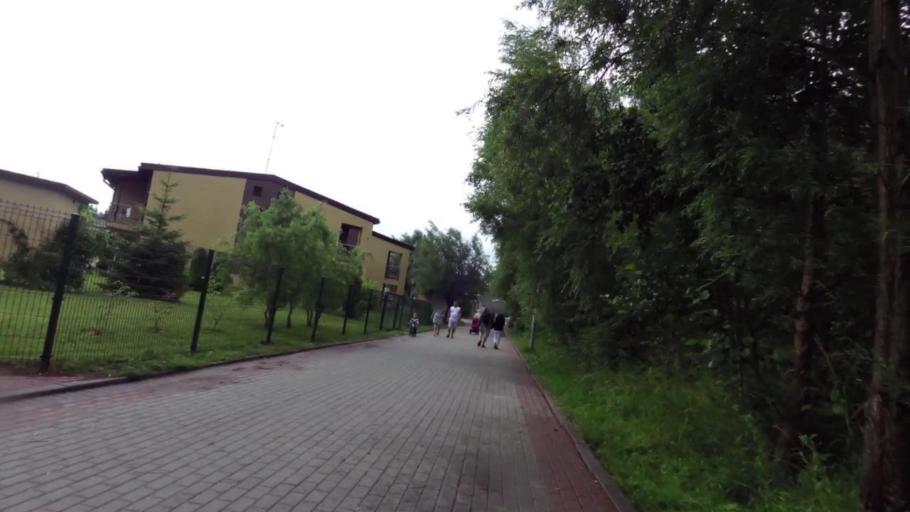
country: PL
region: West Pomeranian Voivodeship
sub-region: Powiat kolobrzeski
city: Ustronie Morskie
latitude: 54.2149
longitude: 15.7491
